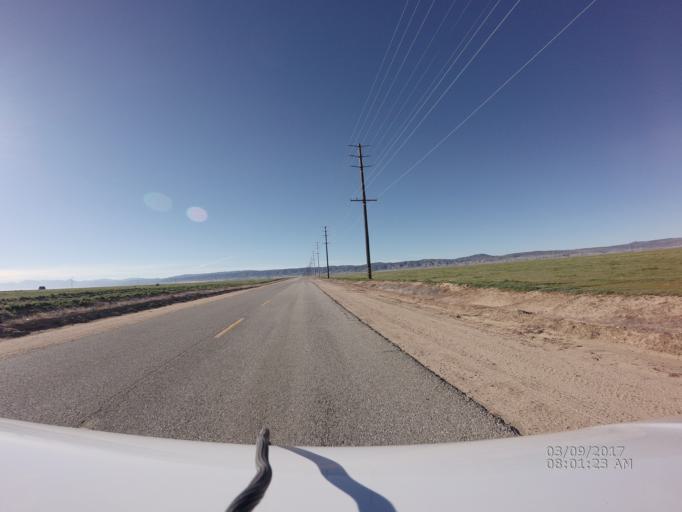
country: US
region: California
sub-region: Los Angeles County
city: Leona Valley
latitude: 34.7524
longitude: -118.3253
